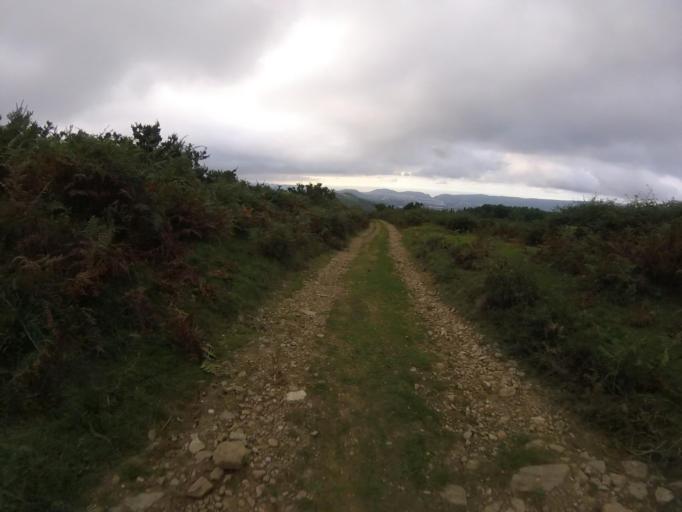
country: ES
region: Basque Country
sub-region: Provincia de Guipuzcoa
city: Irun
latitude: 43.2638
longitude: -1.8307
